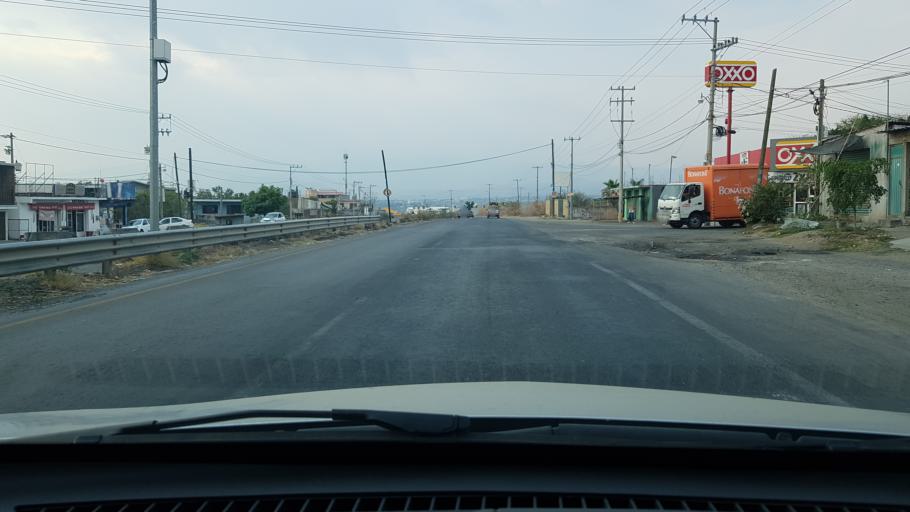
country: MX
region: Morelos
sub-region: Yecapixtla
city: Juan Morales
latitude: 18.8139
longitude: -98.9167
